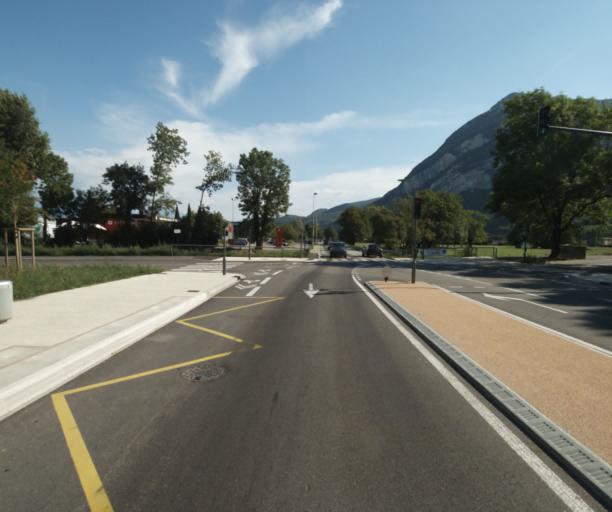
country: FR
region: Rhone-Alpes
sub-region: Departement de l'Isere
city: Sassenage
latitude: 45.2197
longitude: 5.6603
